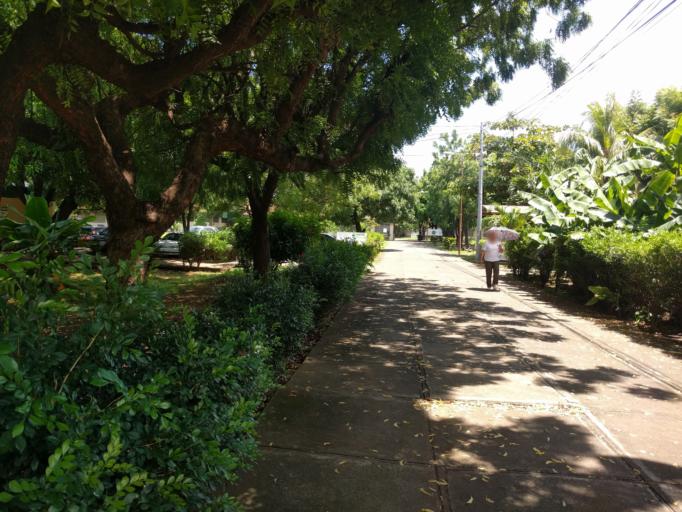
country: NI
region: Managua
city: Managua
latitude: 12.1495
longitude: -86.2482
